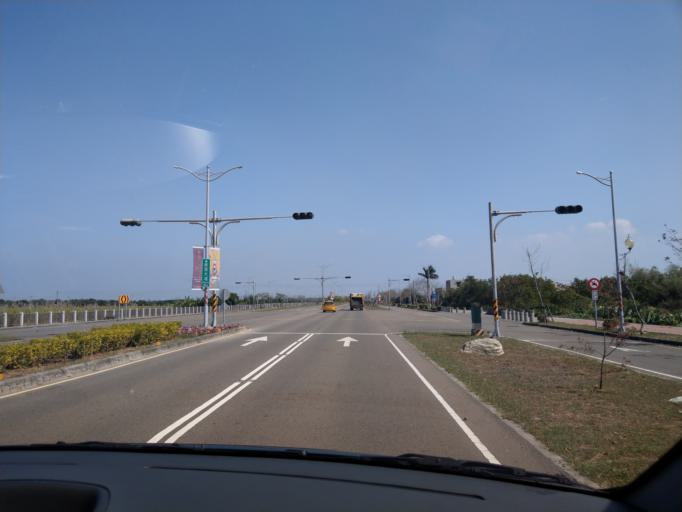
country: TW
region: Taiwan
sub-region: Chiayi
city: Taibao
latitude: 23.4677
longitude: 120.3076
